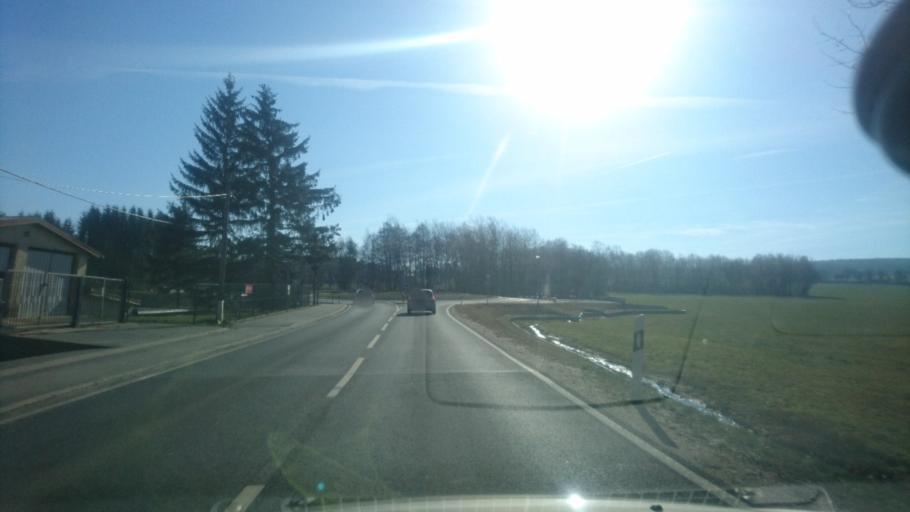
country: DE
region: Saxony
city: Neustadt Vogtland
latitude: 50.4729
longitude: 12.3420
